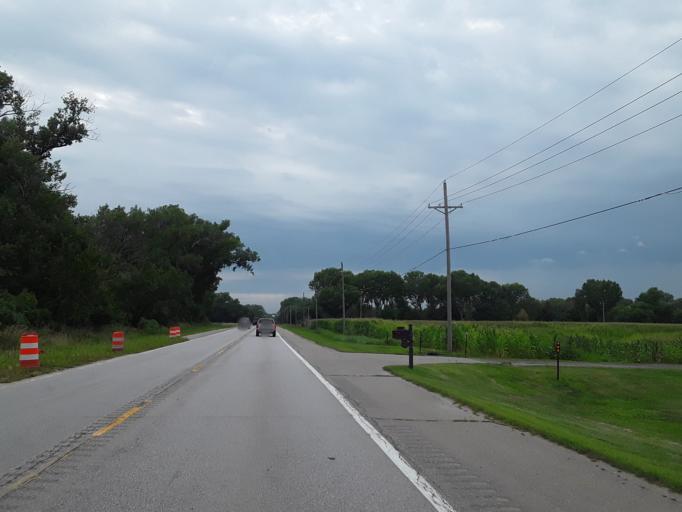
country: US
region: Nebraska
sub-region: Saunders County
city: Yutan
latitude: 41.2338
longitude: -96.3415
